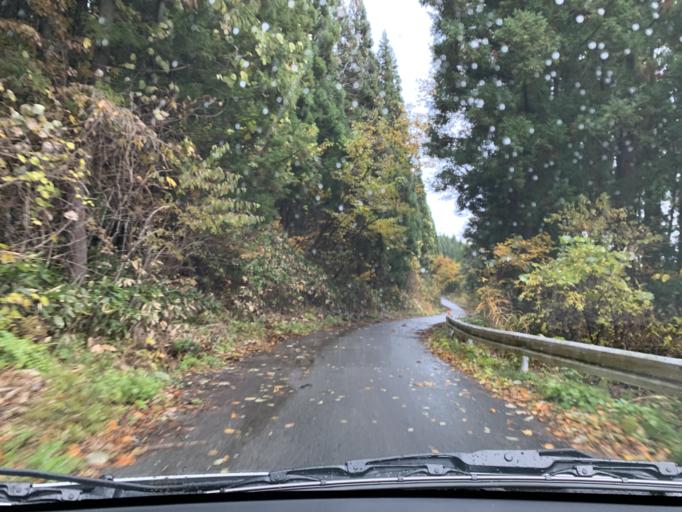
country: JP
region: Iwate
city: Mizusawa
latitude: 39.1034
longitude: 140.9533
